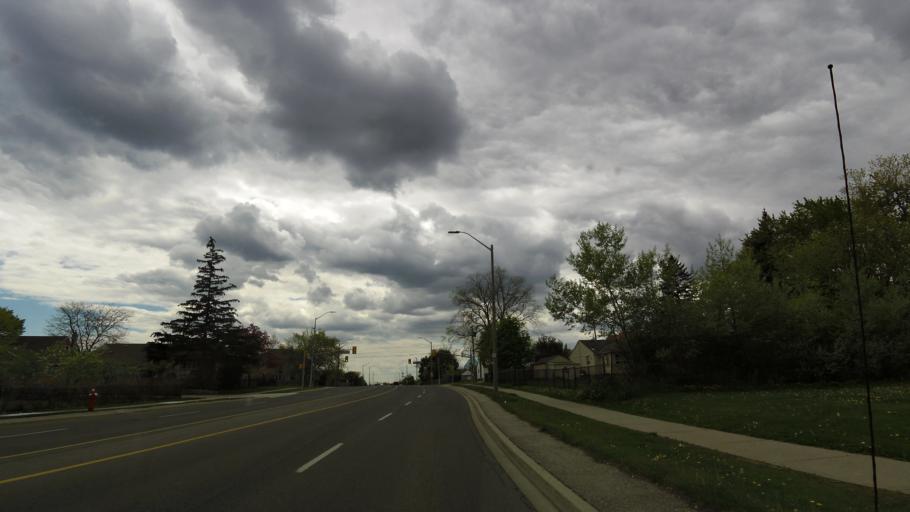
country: CA
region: Ontario
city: Mississauga
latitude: 43.5863
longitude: -79.6322
